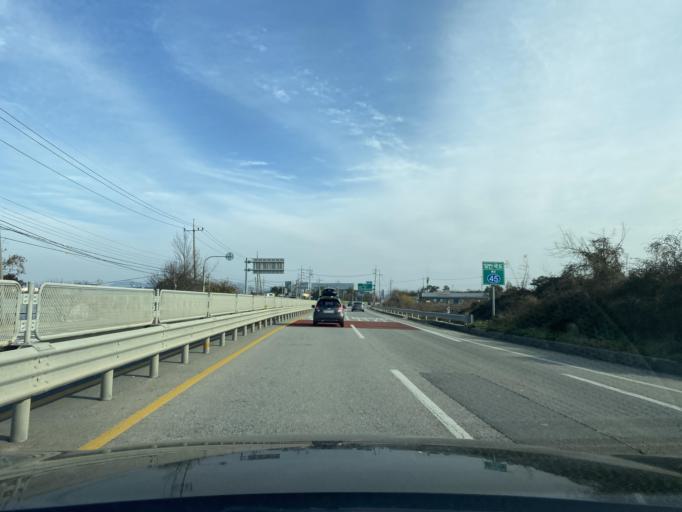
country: KR
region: Chungcheongnam-do
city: Yesan
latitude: 36.6902
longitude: 126.7482
